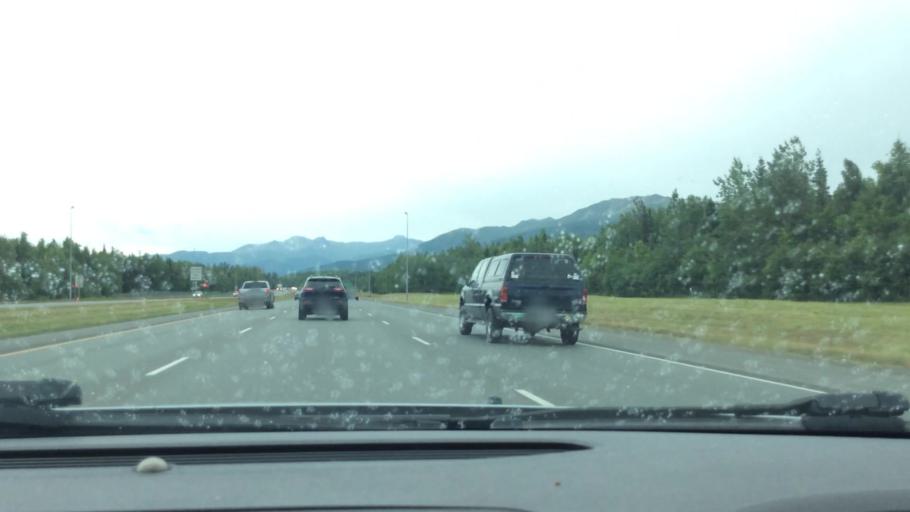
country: US
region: Alaska
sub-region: Anchorage Municipality
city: Elmendorf Air Force Base
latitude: 61.2329
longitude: -149.7076
